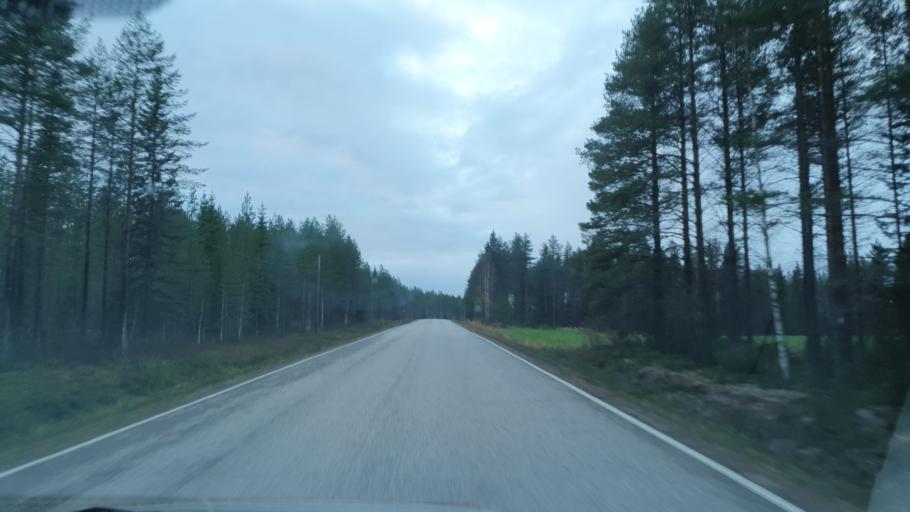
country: FI
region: Kainuu
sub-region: Kajaani
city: Ristijaervi
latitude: 64.4212
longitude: 28.4070
